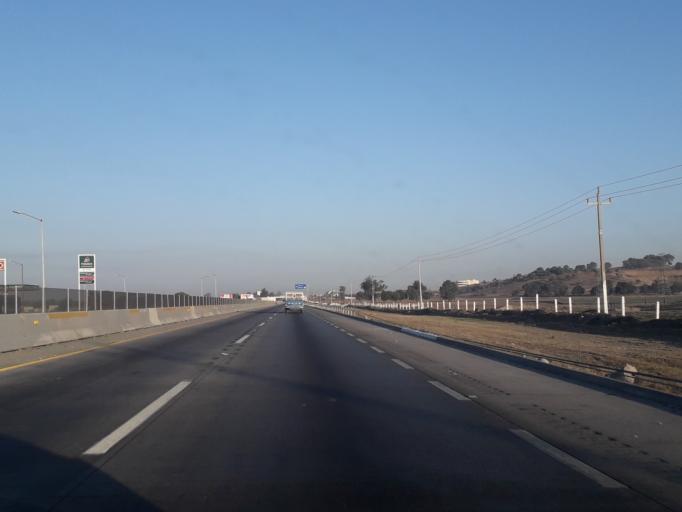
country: MX
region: Puebla
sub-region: Amozoc
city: Amozoc de Mota
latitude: 19.0441
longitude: -98.0123
